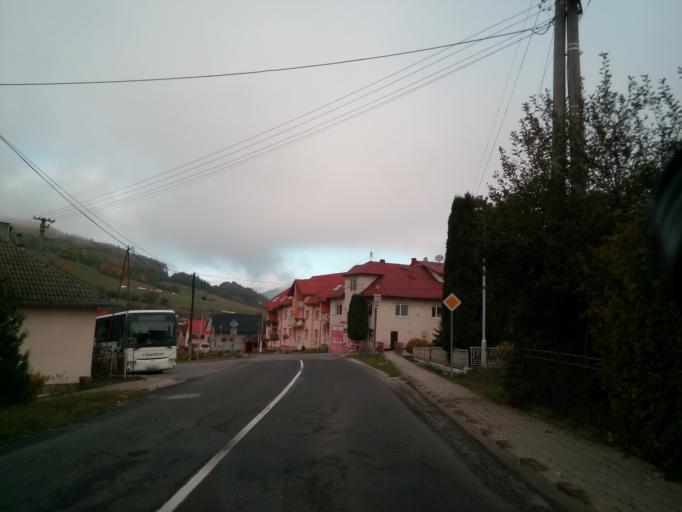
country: SK
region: Kosicky
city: Gelnica
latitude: 48.8556
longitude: 21.0151
